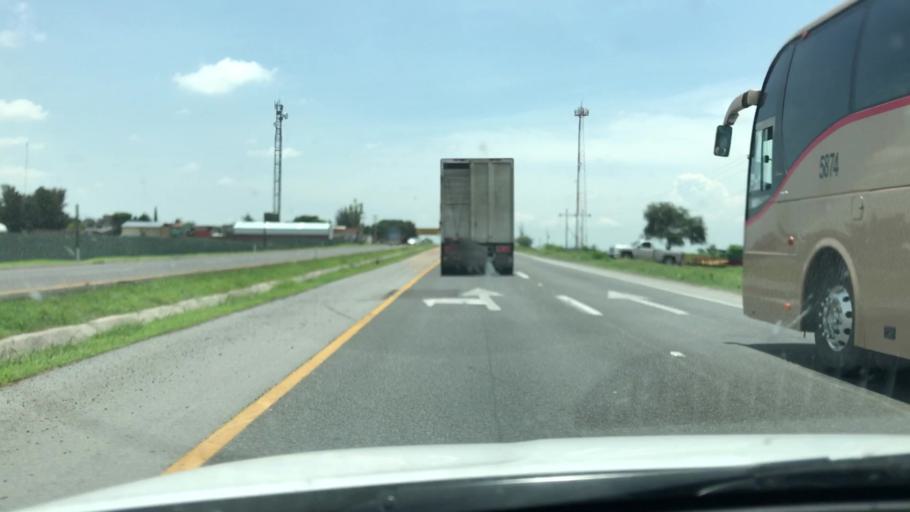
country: MX
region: Guanajuato
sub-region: Penjamo
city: Mezquite de Luna
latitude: 20.3789
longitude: -101.8394
